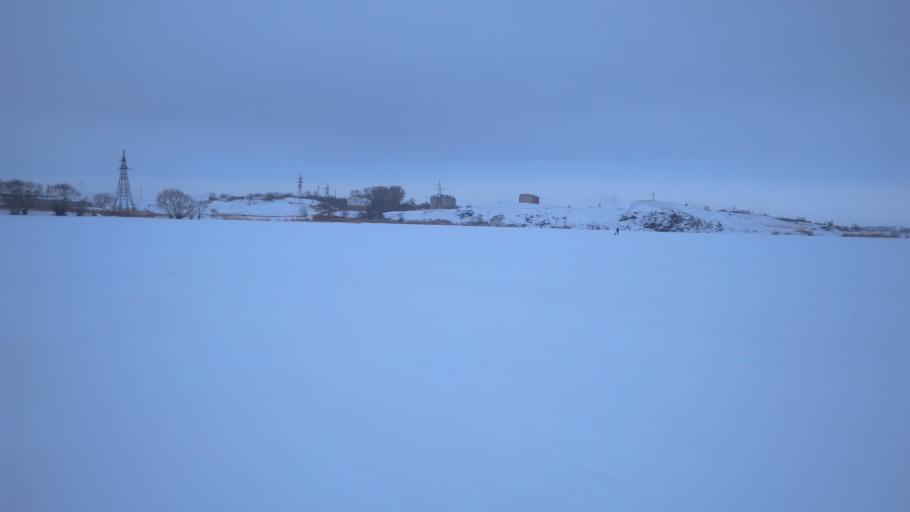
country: RU
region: Chelyabinsk
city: Troitsk
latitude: 54.0818
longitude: 61.5726
